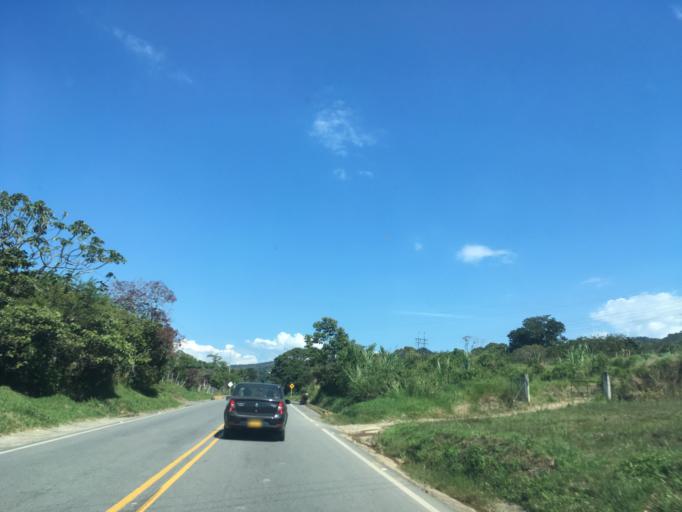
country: CO
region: Santander
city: Suaita
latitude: 6.0757
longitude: -73.4039
